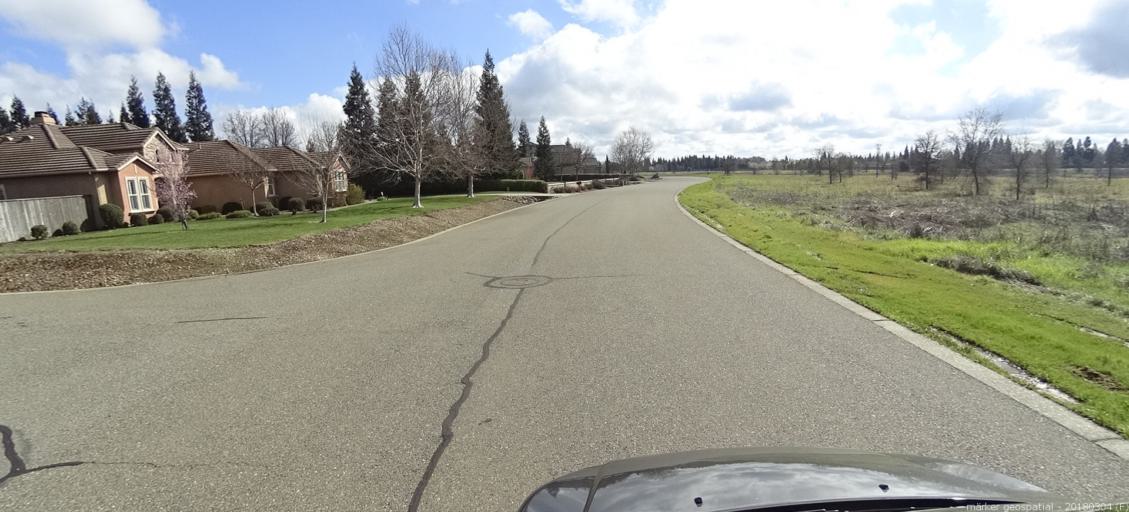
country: US
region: California
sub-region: Sacramento County
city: Vineyard
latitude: 38.4635
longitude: -121.3105
